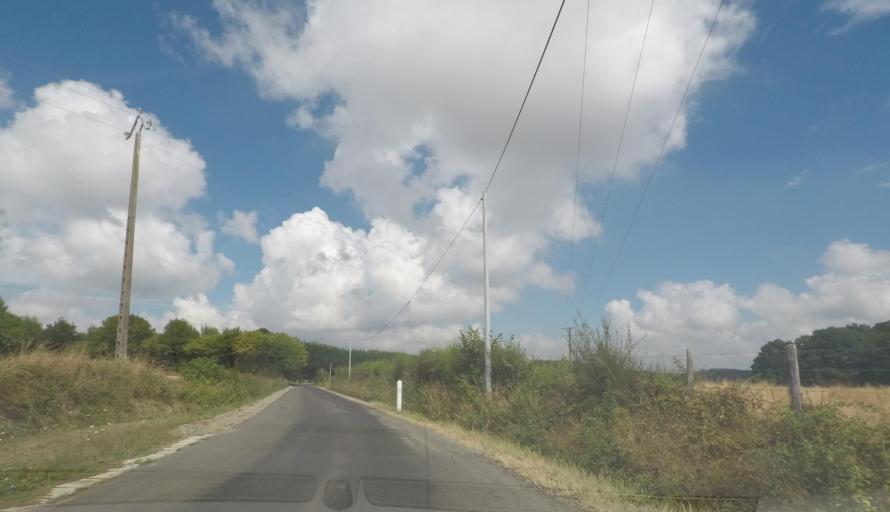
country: FR
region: Pays de la Loire
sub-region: Departement de la Sarthe
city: Saint-Cosme-en-Vairais
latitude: 48.2619
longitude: 0.5371
